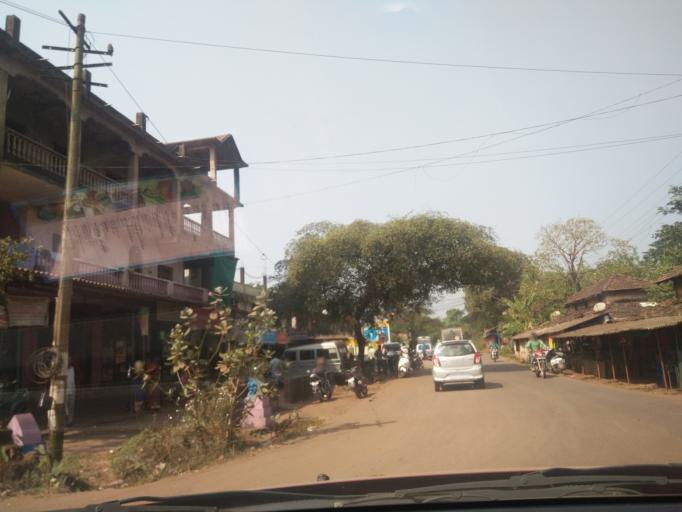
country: IN
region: Goa
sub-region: North Goa
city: Sanquelim
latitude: 15.5484
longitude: 74.0447
